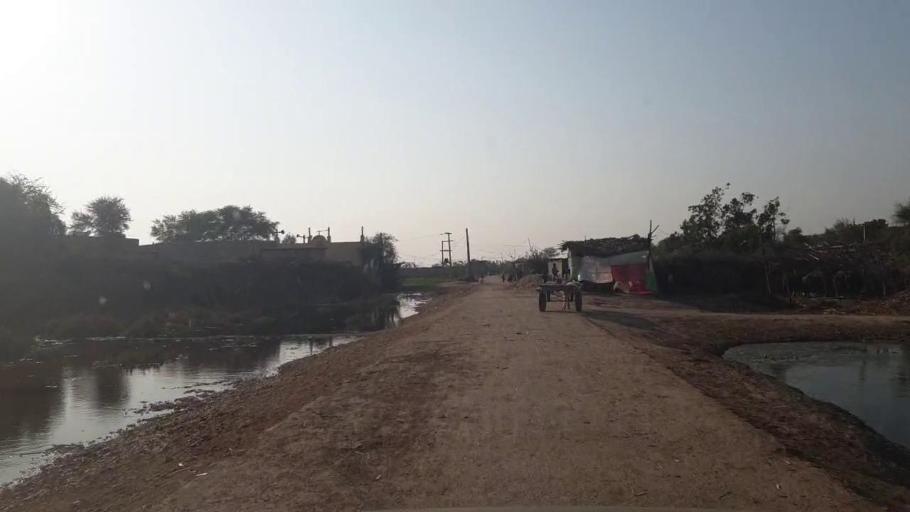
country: PK
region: Sindh
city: Bhit Shah
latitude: 25.8335
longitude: 68.5200
